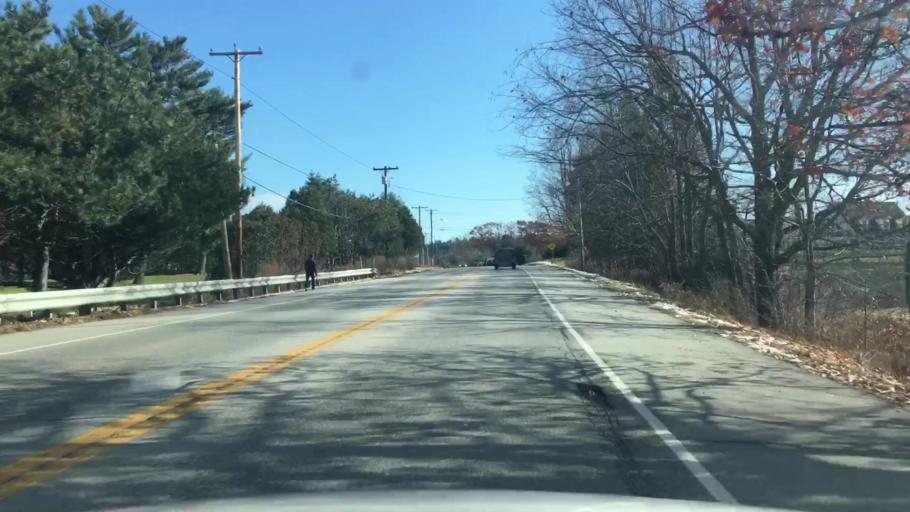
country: US
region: Maine
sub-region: Kennebec County
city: Manchester
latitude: 44.3245
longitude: -69.8790
